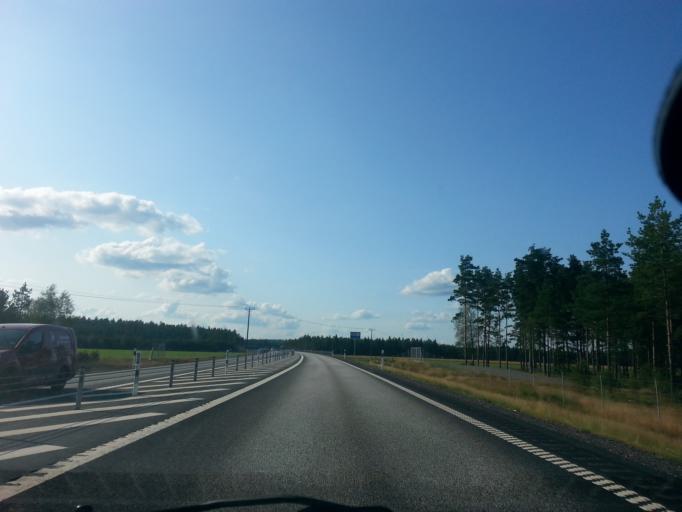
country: SE
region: Joenkoeping
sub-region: Gislaveds Kommun
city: Gislaved
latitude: 57.3118
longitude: 13.5725
